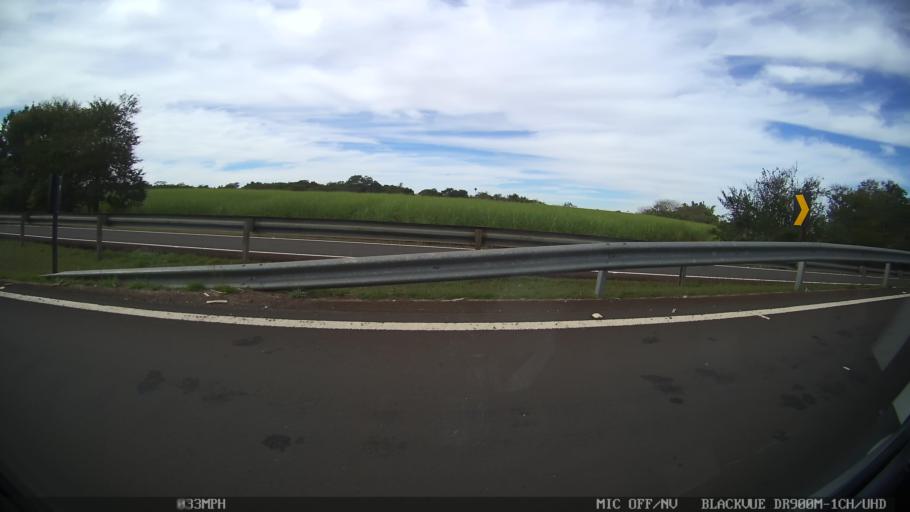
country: BR
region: Sao Paulo
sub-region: Taquaritinga
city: Taquaritinga
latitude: -21.4758
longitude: -48.5963
